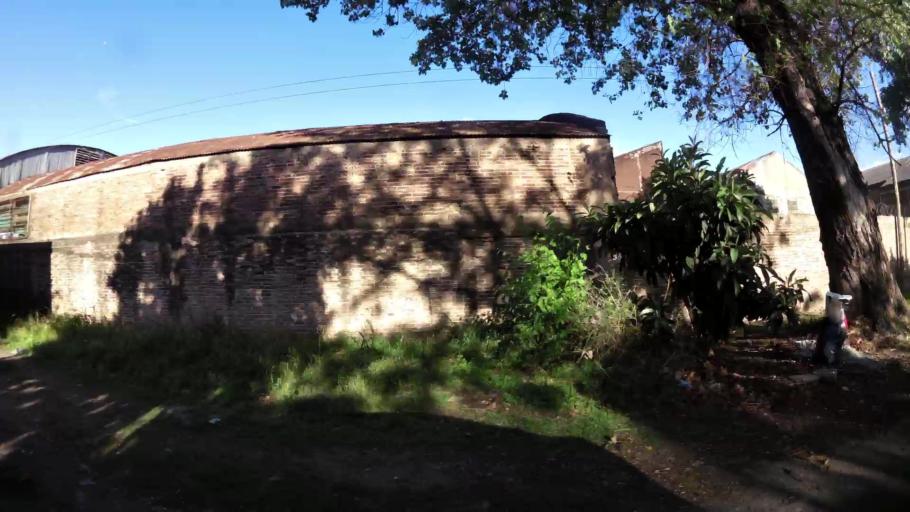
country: AR
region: Santa Fe
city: Gobernador Galvez
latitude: -32.9924
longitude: -60.6752
